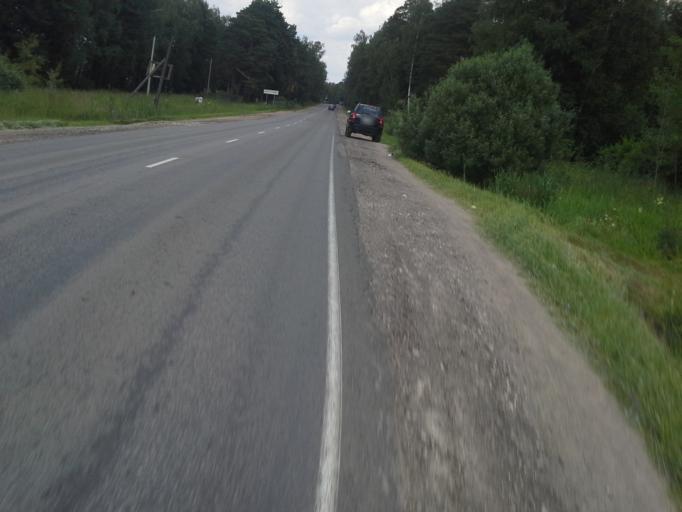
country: RU
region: Moskovskaya
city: Kievskij
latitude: 55.4133
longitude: 36.8057
